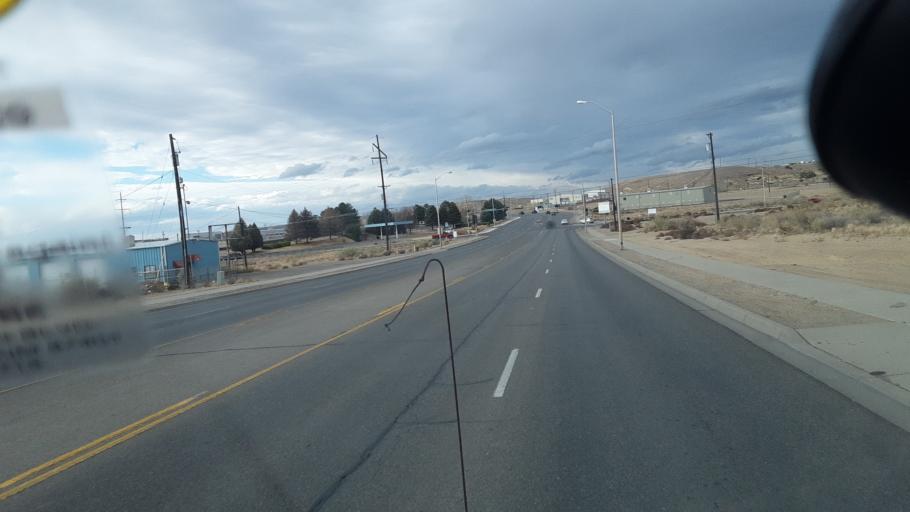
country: US
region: New Mexico
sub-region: San Juan County
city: Farmington
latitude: 36.7255
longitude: -108.1596
